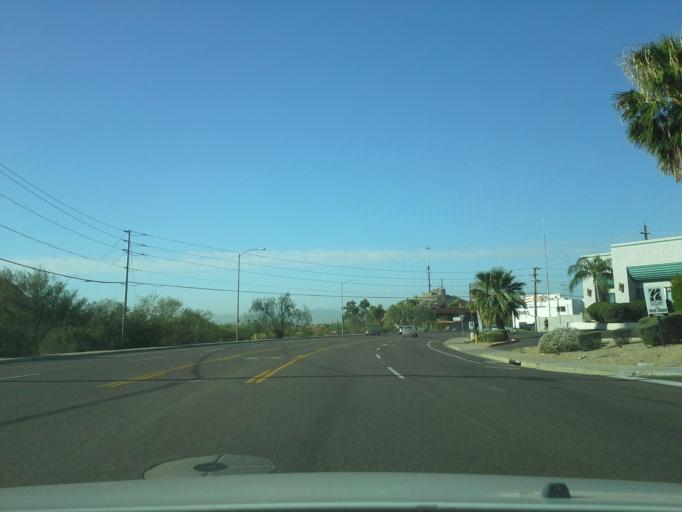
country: US
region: Arizona
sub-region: Maricopa County
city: Paradise Valley
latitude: 33.5914
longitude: -112.0433
